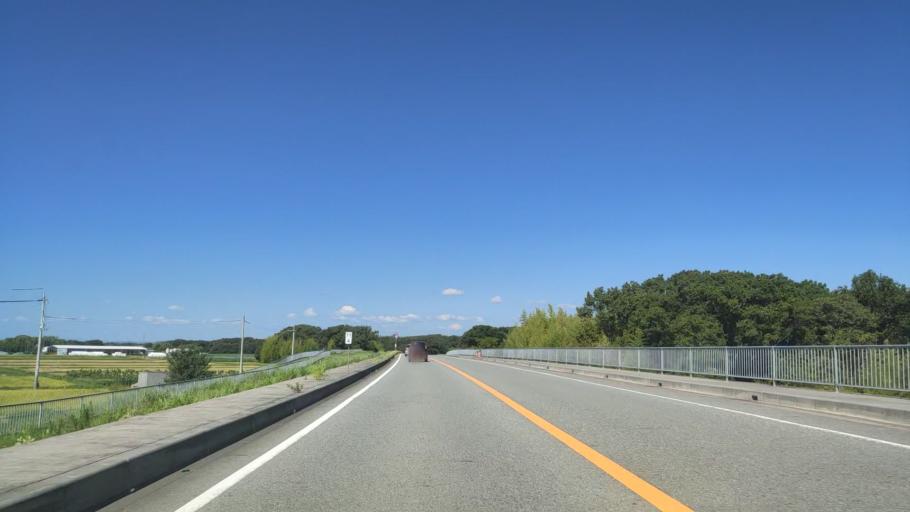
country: JP
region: Hyogo
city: Miki
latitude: 34.7535
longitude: 134.9809
